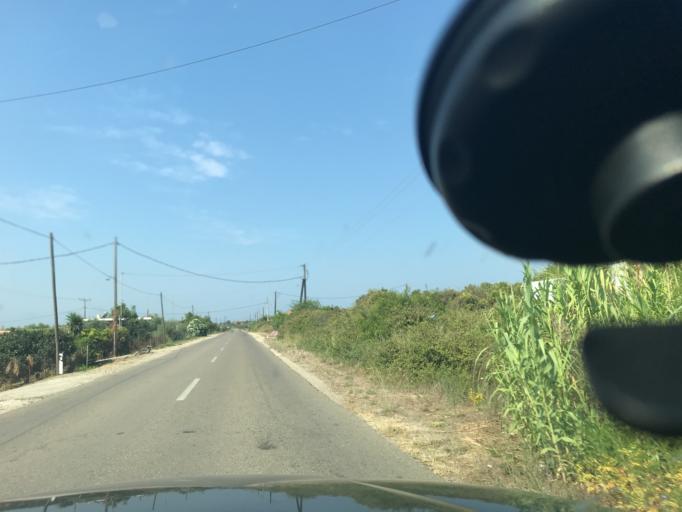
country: GR
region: West Greece
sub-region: Nomos Ileias
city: Kardamas
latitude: 37.7217
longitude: 21.3626
